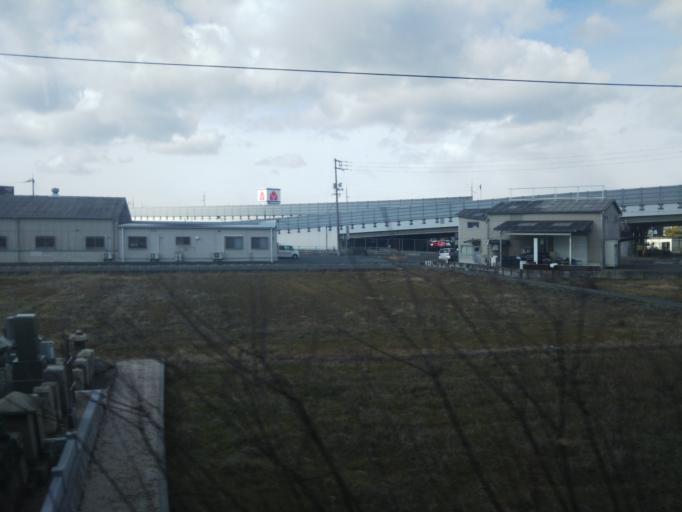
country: JP
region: Okayama
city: Okayama-shi
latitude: 34.6253
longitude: 133.8935
